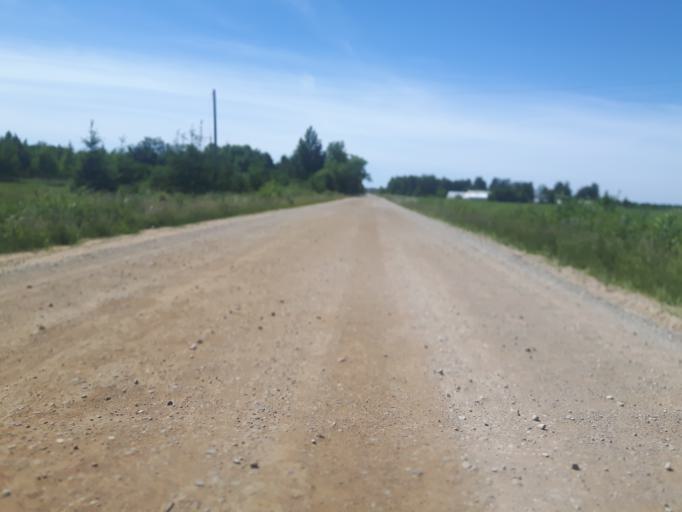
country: LV
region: Grobina
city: Grobina
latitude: 56.5281
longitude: 21.1393
